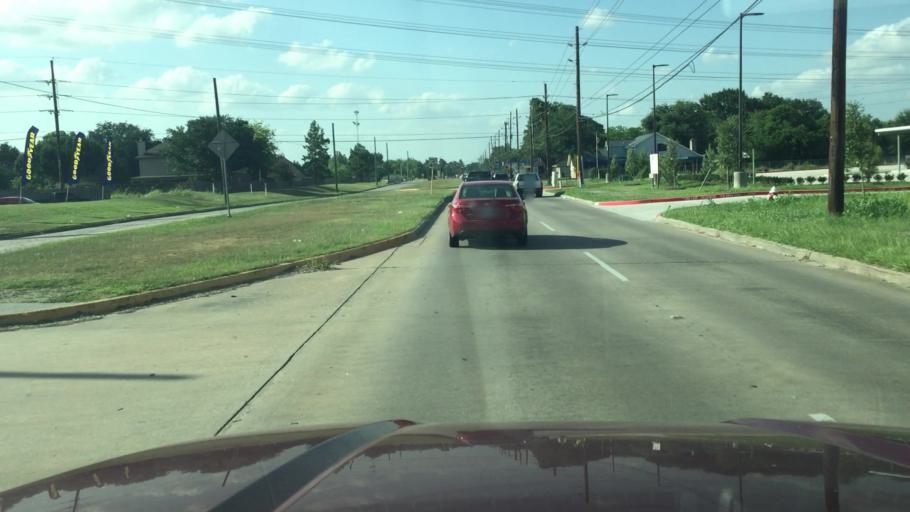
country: US
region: Texas
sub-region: Harris County
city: Hudson
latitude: 29.9535
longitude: -95.4983
